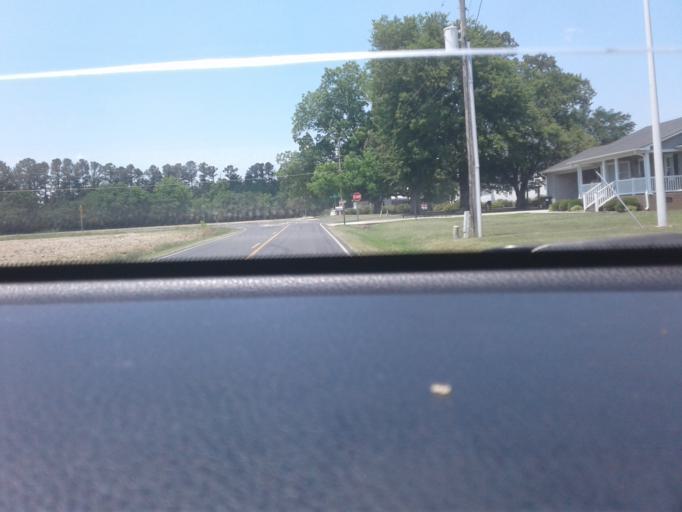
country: US
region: North Carolina
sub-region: Harnett County
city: Dunn
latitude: 35.3428
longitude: -78.5780
